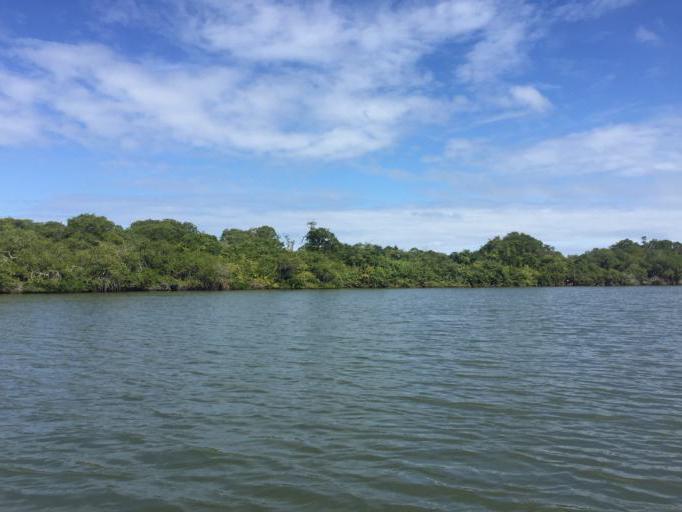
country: MX
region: Veracruz
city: Tecolutla
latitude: 20.4648
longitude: -97.0049
